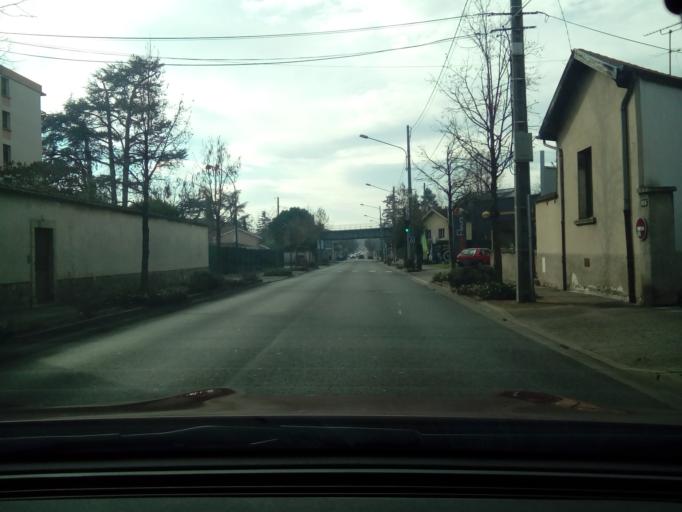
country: FR
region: Rhone-Alpes
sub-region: Departement du Rhone
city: Tassin-la-Demi-Lune
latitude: 45.7559
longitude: 4.7721
